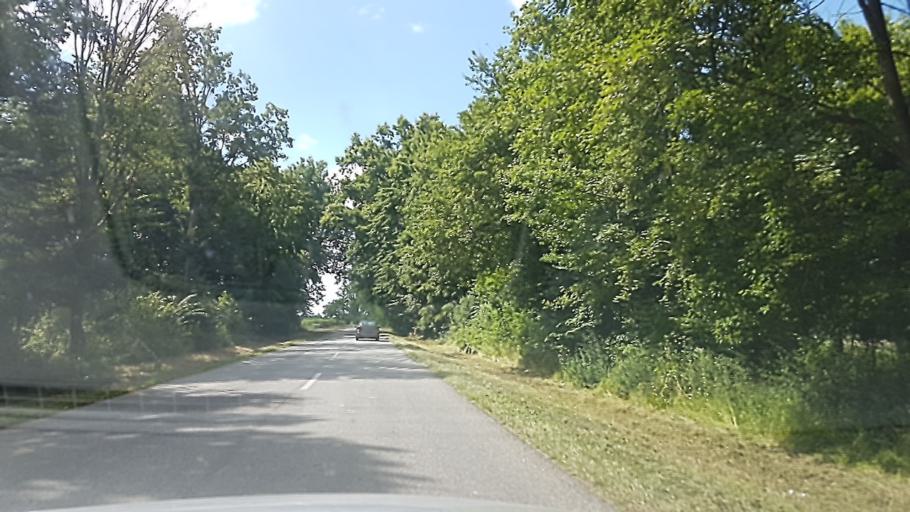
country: HU
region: Somogy
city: Barcs
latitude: 45.9479
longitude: 17.6283
